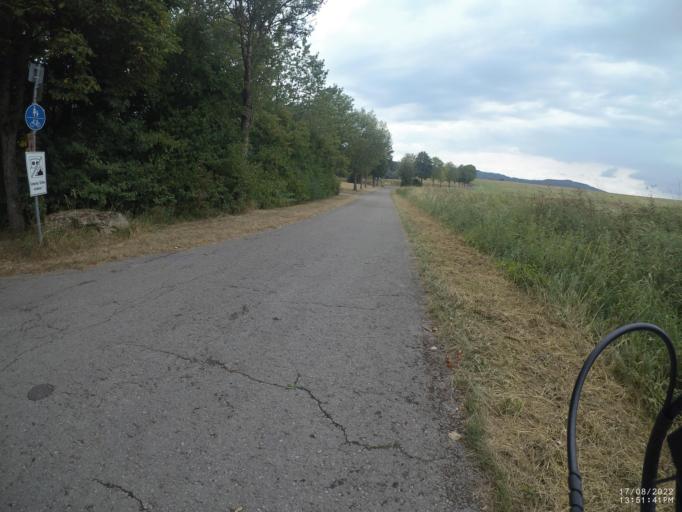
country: DE
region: Rheinland-Pfalz
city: Hillesheim
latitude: 50.2878
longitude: 6.6637
